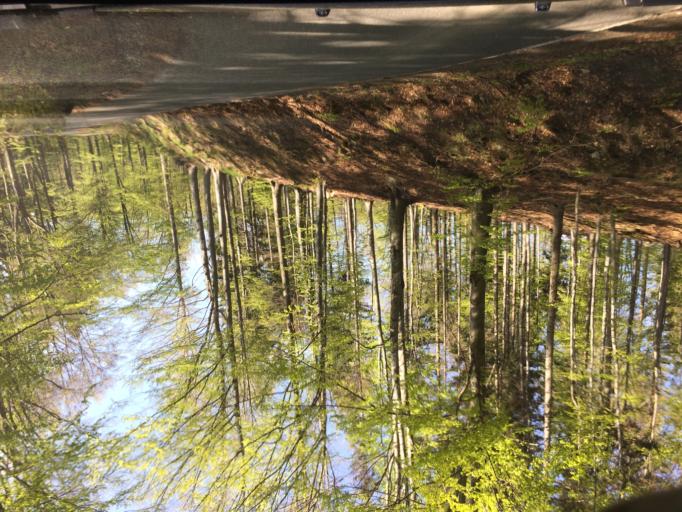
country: PL
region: Lower Silesian Voivodeship
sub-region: Powiat klodzki
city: Jugow
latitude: 50.6703
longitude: 16.5181
